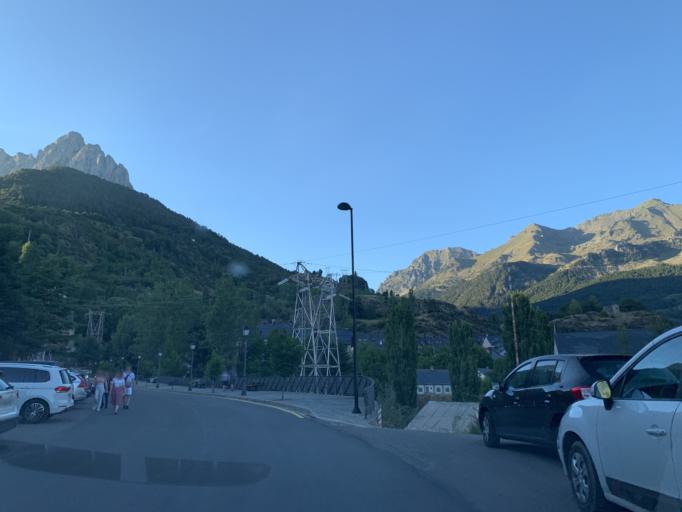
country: ES
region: Aragon
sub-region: Provincia de Huesca
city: Sallent de Gallego
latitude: 42.7701
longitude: -0.3343
